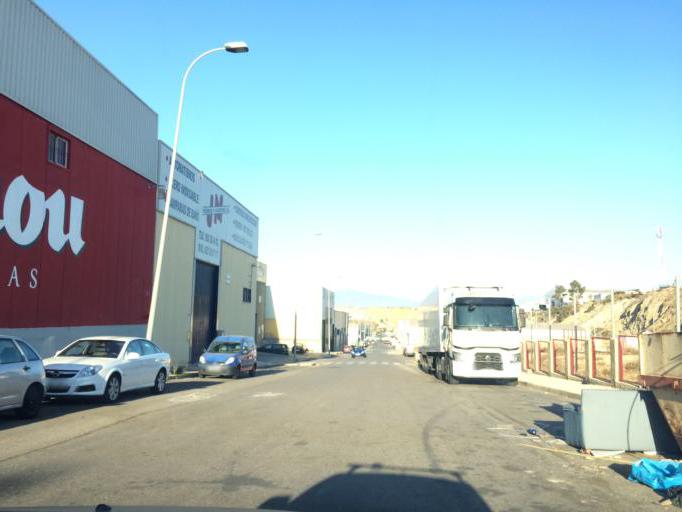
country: ES
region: Andalusia
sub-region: Provincia de Almeria
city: Viator
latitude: 36.8826
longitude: -2.4145
